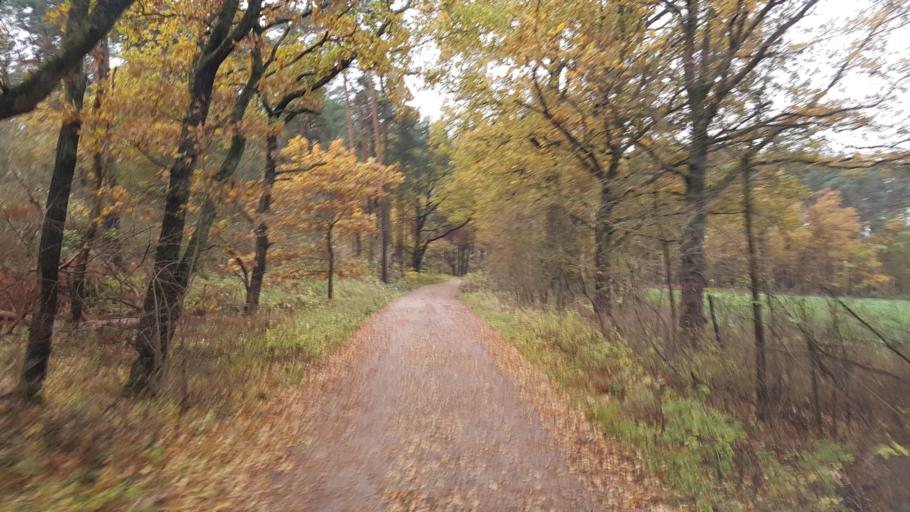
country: DE
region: Brandenburg
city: Drebkau
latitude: 51.6917
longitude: 14.2237
